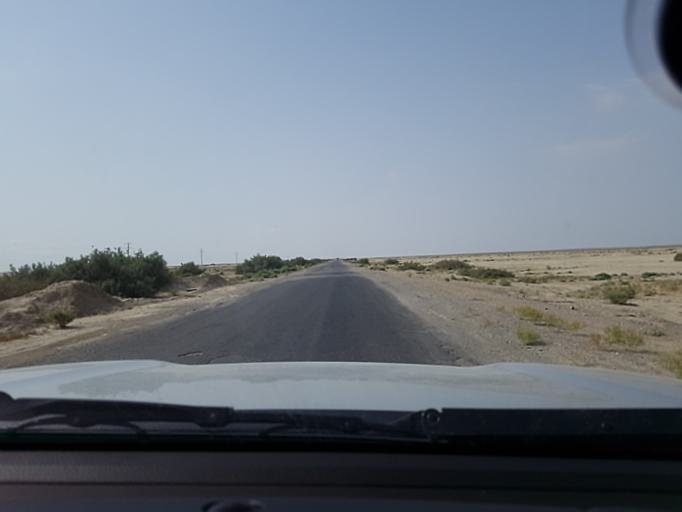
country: TM
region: Balkan
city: Gumdag
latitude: 38.9764
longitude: 54.5877
